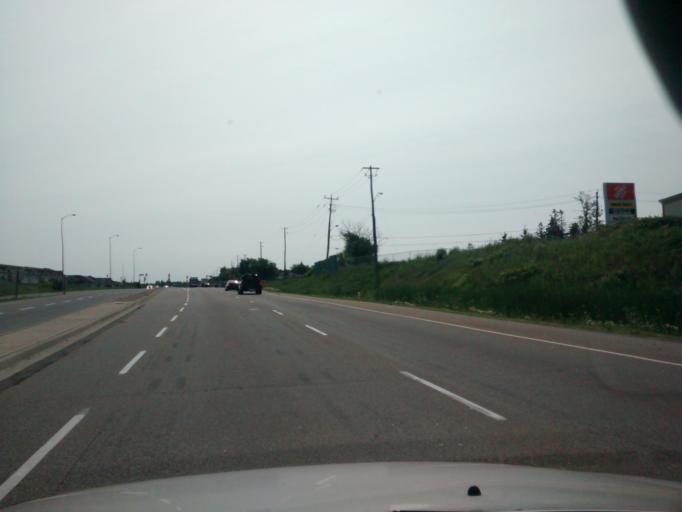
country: CA
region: Ontario
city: Hamilton
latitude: 43.1963
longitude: -79.8102
